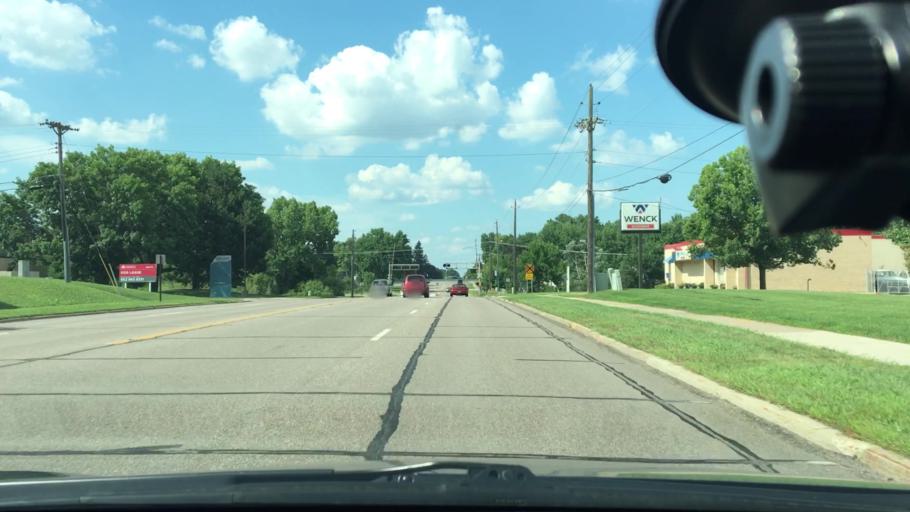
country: US
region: Minnesota
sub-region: Hennepin County
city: New Hope
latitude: 45.0470
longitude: -93.3803
